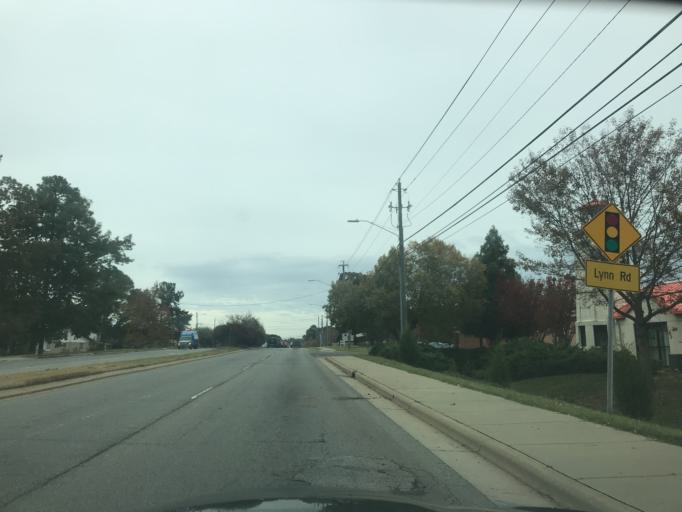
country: US
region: North Carolina
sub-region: Wake County
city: West Raleigh
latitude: 35.8704
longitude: -78.6798
